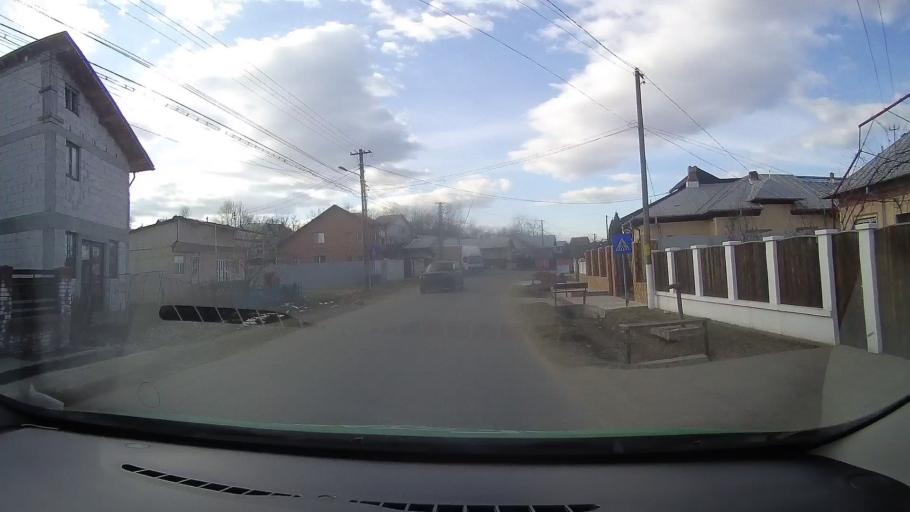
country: RO
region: Dambovita
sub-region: Comuna Ulmi
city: Ulmi
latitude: 44.8848
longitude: 25.5114
